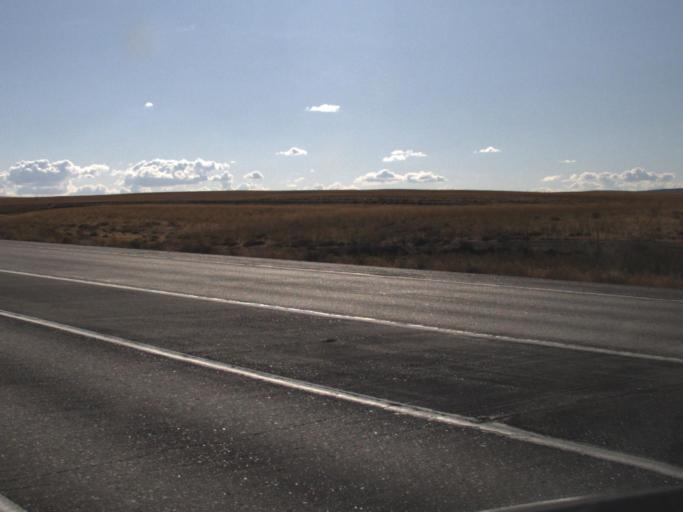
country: US
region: Washington
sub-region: Benton County
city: Kennewick
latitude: 46.1556
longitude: -119.2021
